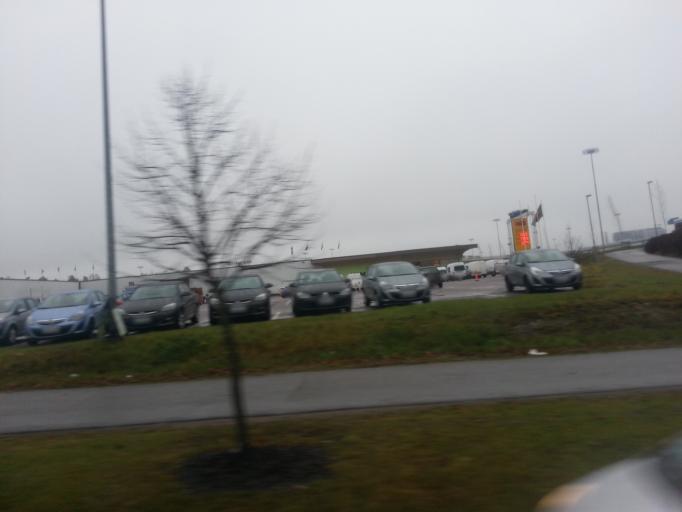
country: FI
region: Uusimaa
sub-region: Helsinki
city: Vantaa
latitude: 60.2962
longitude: 24.9511
